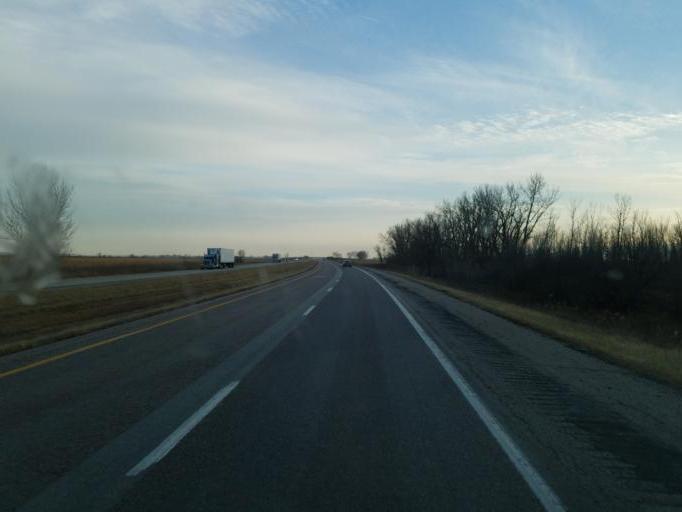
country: US
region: Nebraska
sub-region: Washington County
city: Blair
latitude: 41.6812
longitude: -96.0408
